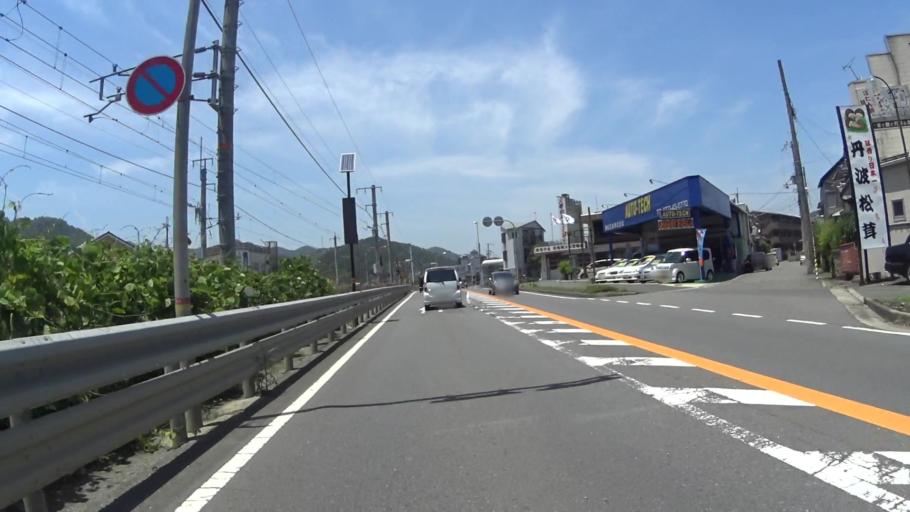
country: JP
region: Kyoto
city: Kameoka
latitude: 35.0669
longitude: 135.5382
